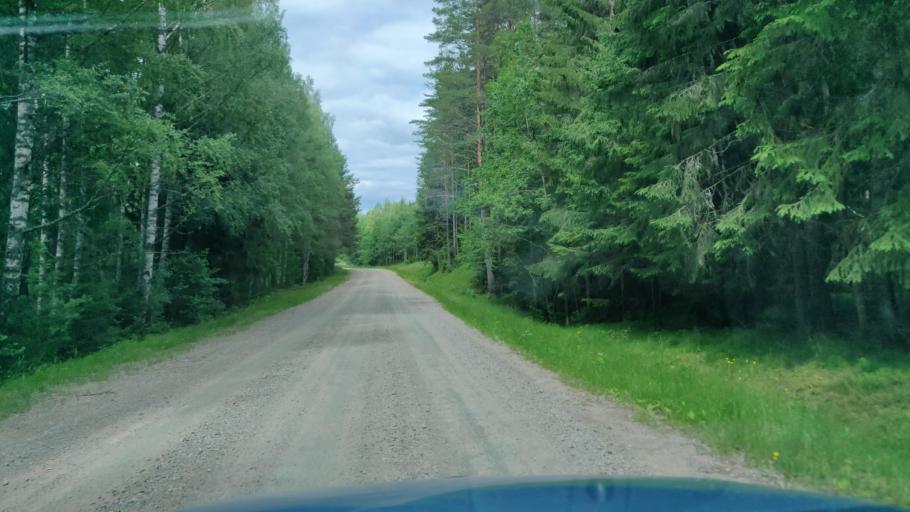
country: SE
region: Vaermland
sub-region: Hagfors Kommun
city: Hagfors
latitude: 60.0366
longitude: 13.7205
